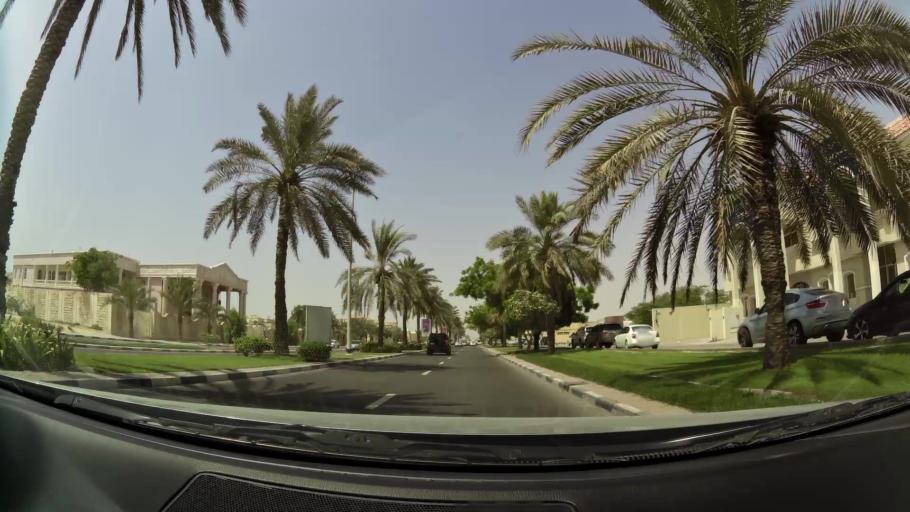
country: AE
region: Dubai
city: Dubai
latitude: 25.1369
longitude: 55.2021
